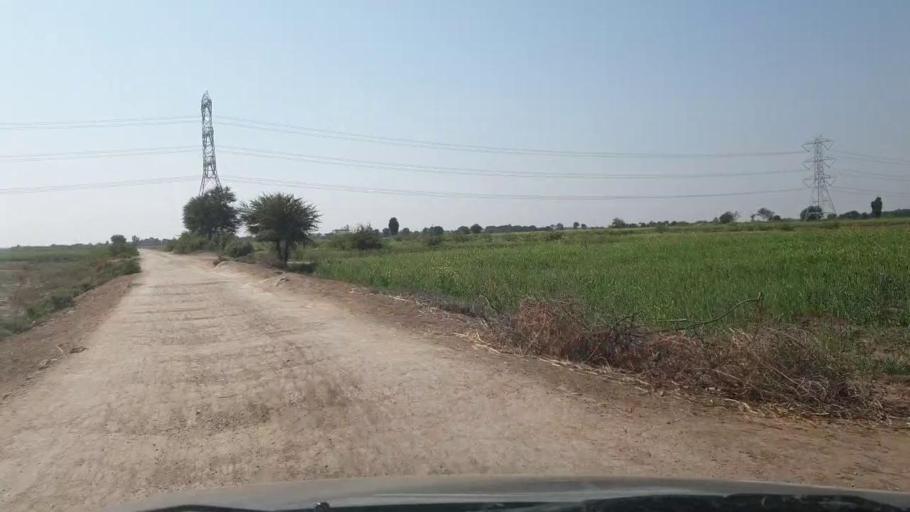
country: PK
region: Sindh
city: Digri
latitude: 25.1881
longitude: 69.2187
